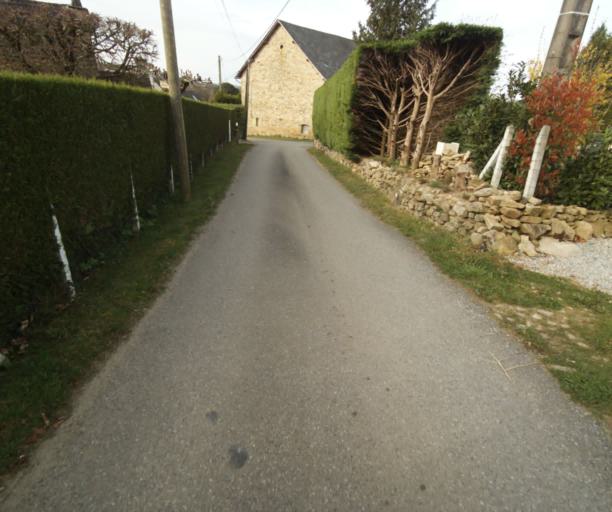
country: FR
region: Limousin
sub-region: Departement de la Correze
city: Chamboulive
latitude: 45.4482
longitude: 1.7784
